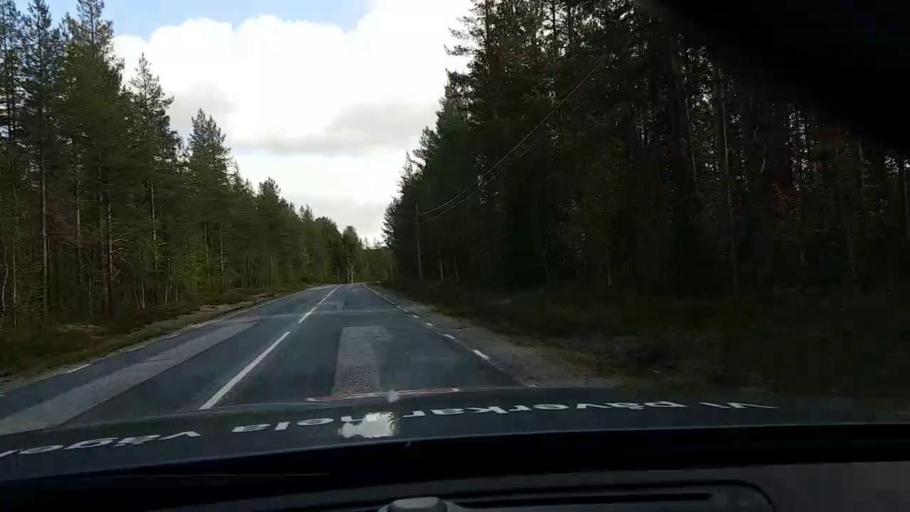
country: SE
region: Vaesterbotten
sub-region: Asele Kommun
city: Asele
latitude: 63.7924
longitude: 17.5801
